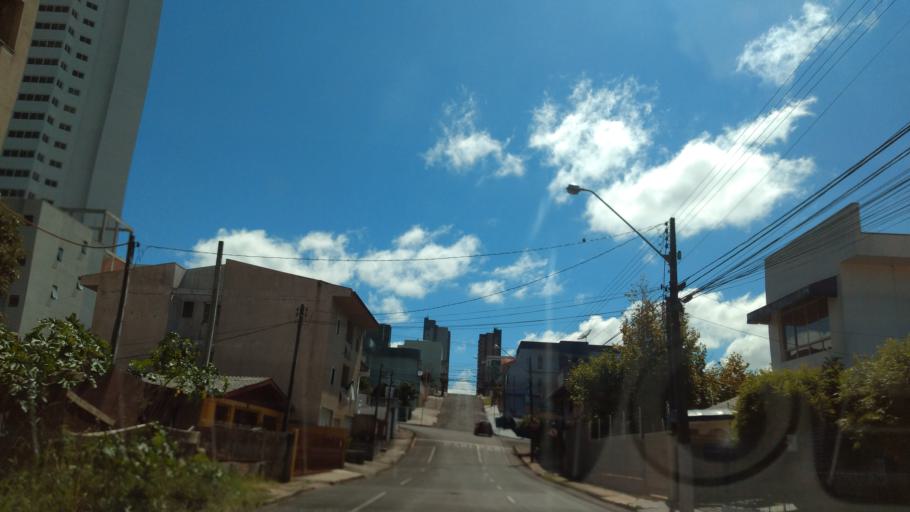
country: BR
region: Parana
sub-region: Guarapuava
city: Guarapuava
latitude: -25.3982
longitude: -51.4688
